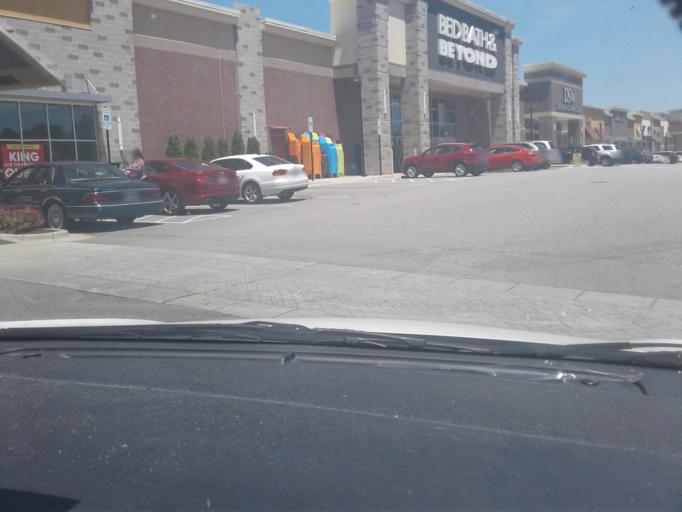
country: US
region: North Carolina
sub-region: Wake County
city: Holly Springs
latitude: 35.6644
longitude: -78.8466
